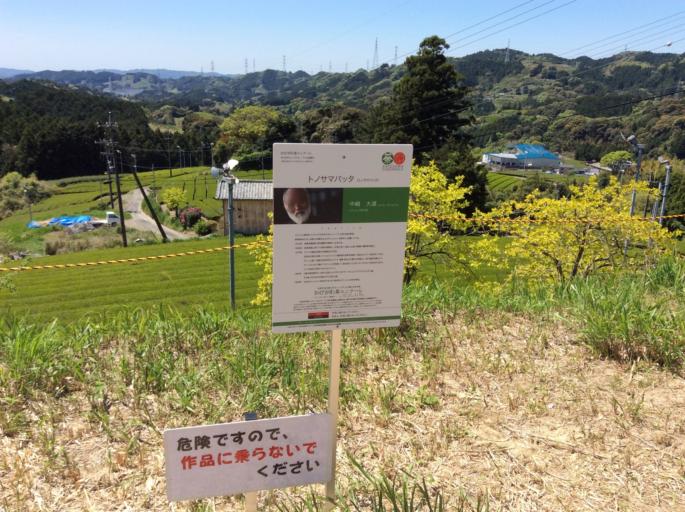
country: JP
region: Shizuoka
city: Kanaya
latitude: 34.8363
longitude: 138.0815
